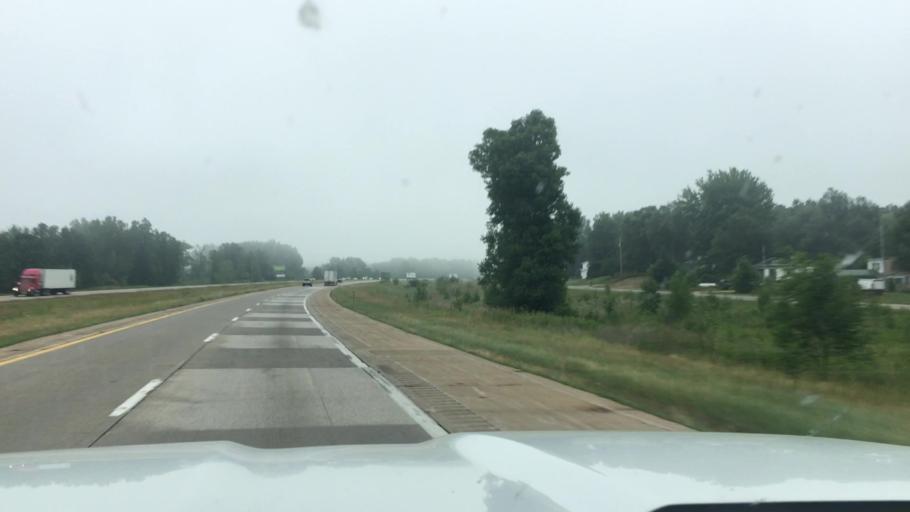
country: US
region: Michigan
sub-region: Shiawassee County
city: Perry
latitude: 42.8231
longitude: -84.2667
